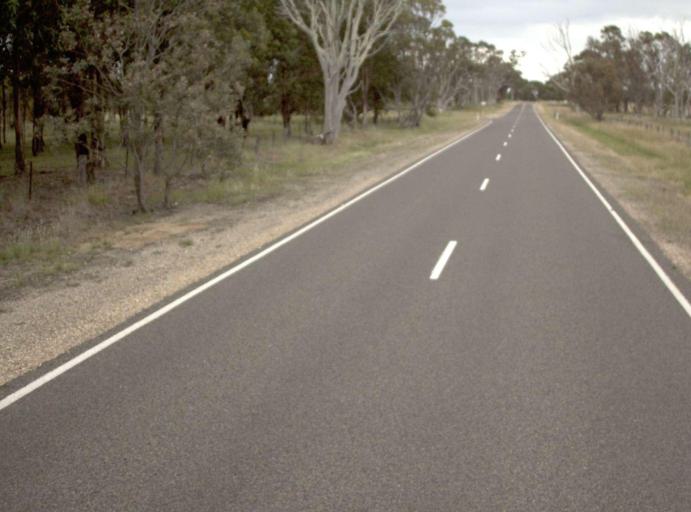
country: AU
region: Victoria
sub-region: East Gippsland
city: Bairnsdale
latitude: -37.9675
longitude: 147.4810
